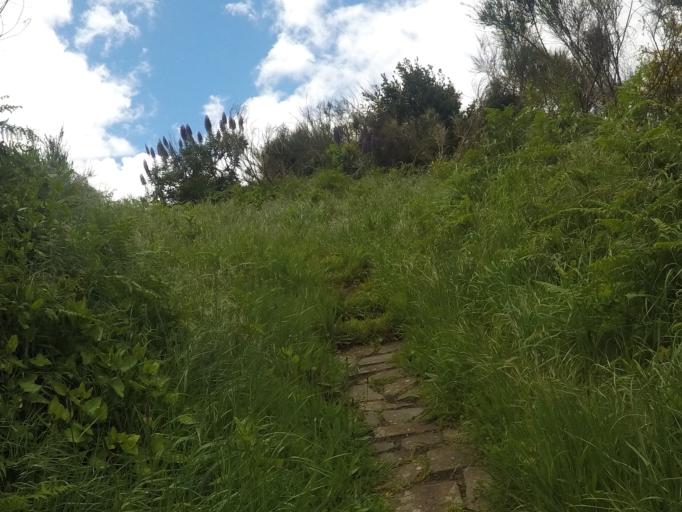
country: PT
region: Madeira
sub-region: Camara de Lobos
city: Curral das Freiras
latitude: 32.7400
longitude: -17.0066
